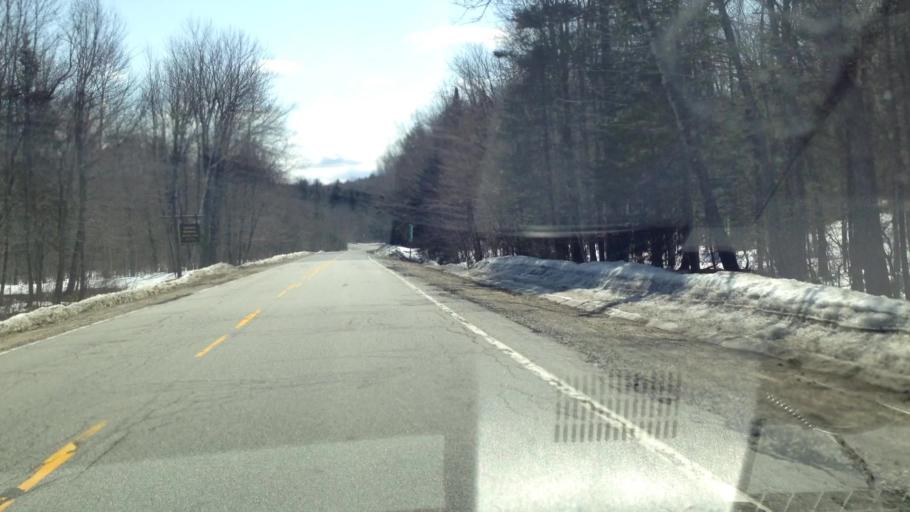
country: US
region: New Hampshire
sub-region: Sullivan County
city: Springfield
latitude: 43.4837
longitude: -71.9761
